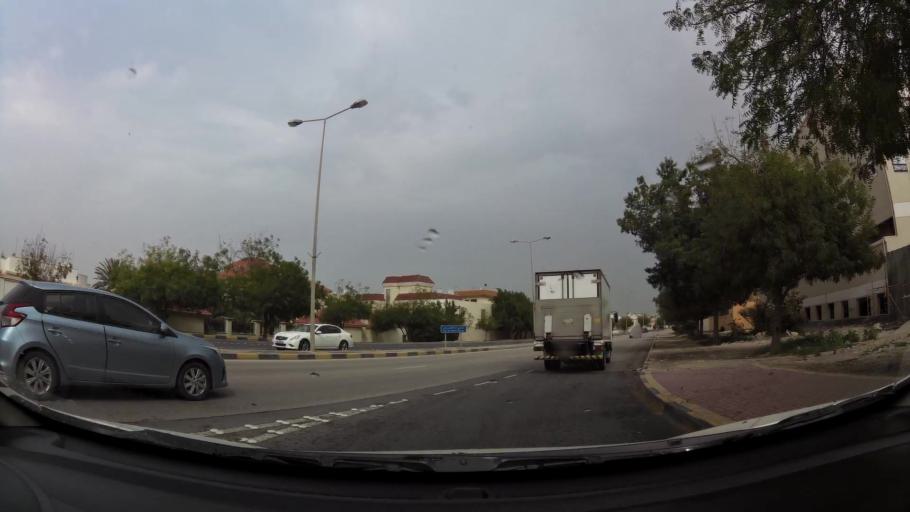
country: BH
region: Northern
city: Ar Rifa'
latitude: 26.1405
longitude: 50.5588
